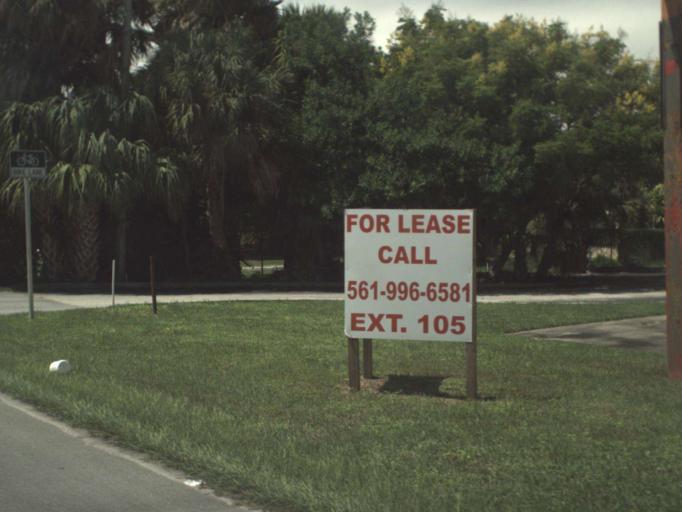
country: US
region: Florida
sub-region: Palm Beach County
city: Pahokee
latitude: 26.8257
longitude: -80.6627
